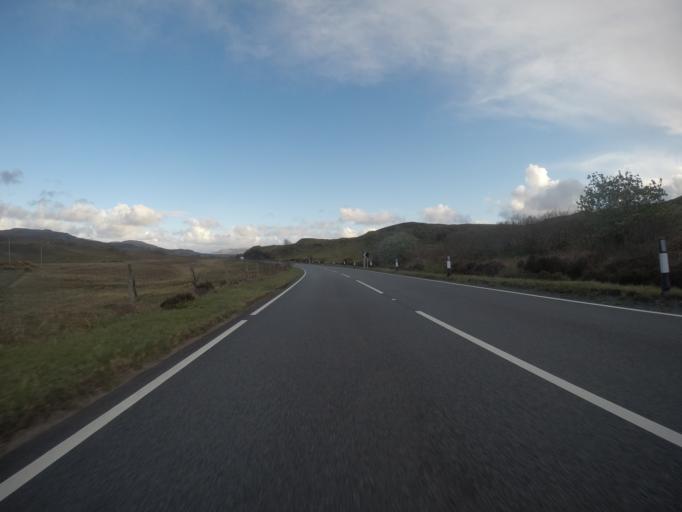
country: GB
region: Scotland
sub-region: Highland
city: Isle of Skye
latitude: 57.5113
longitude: -6.3403
